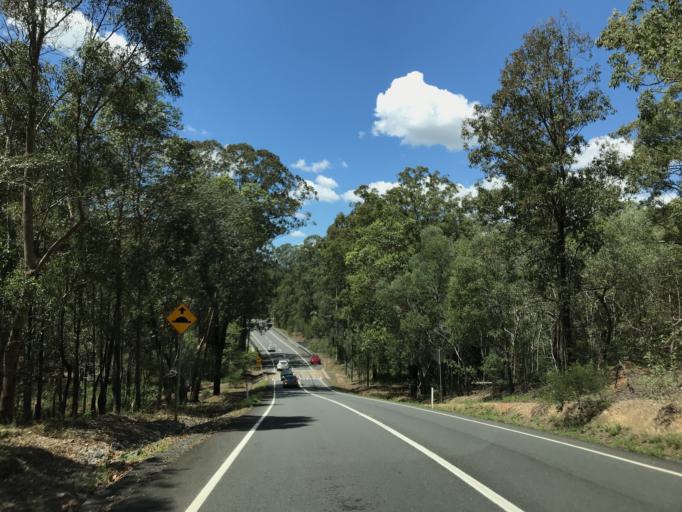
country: AU
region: Queensland
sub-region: Brisbane
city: Kenmore Hills
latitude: -27.4759
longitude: 152.9250
